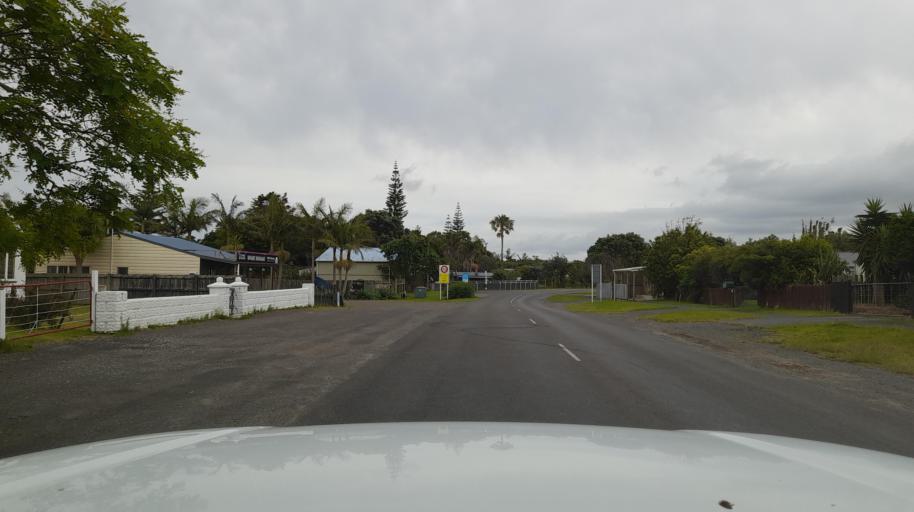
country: NZ
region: Northland
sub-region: Far North District
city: Ahipara
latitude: -35.1705
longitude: 173.1531
